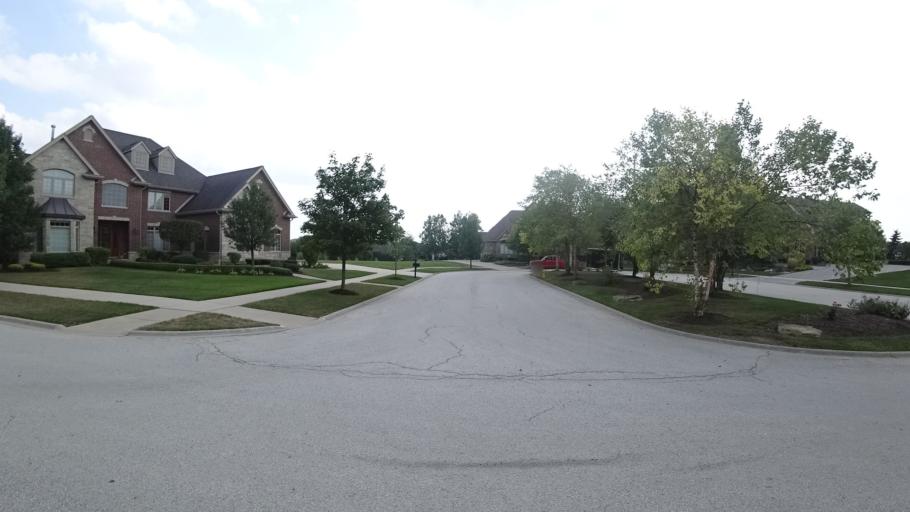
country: US
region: Illinois
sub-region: Cook County
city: Orland Park
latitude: 41.6346
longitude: -87.8892
